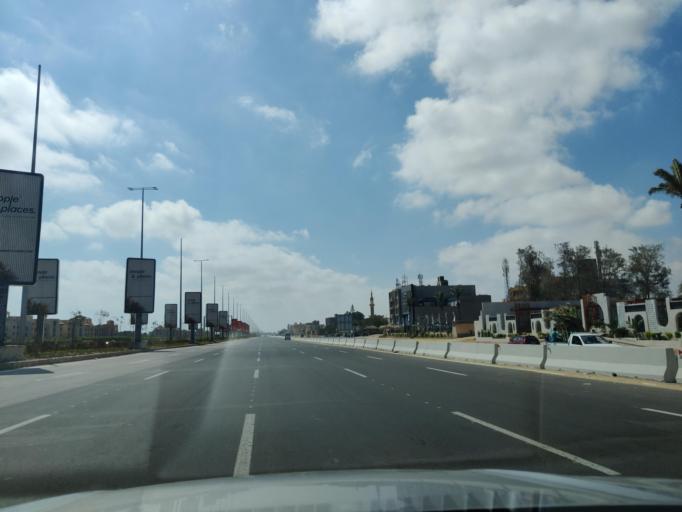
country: EG
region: Muhafazat Matruh
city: Al `Alamayn
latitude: 30.9683
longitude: 28.7438
